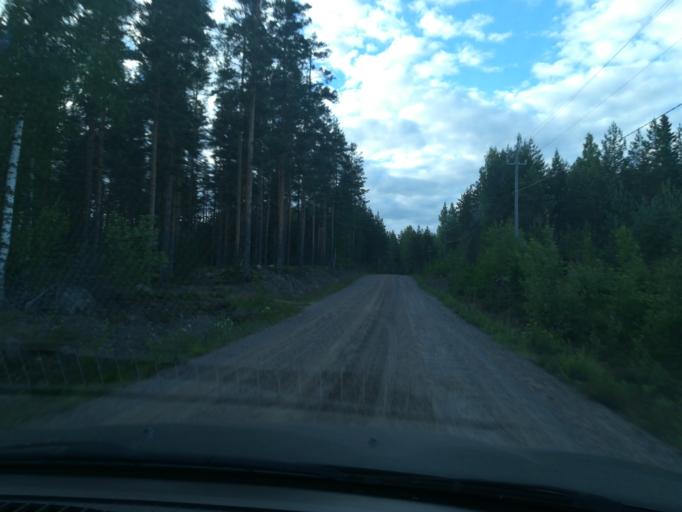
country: FI
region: Southern Savonia
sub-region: Mikkeli
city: Puumala
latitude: 61.6018
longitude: 28.1502
